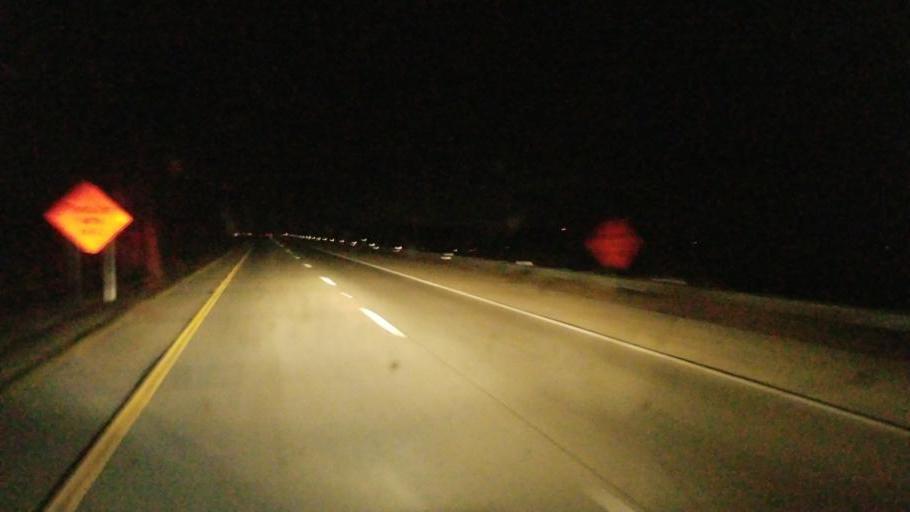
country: US
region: Ohio
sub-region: Allen County
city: Bluffton
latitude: 40.8268
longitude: -83.9041
